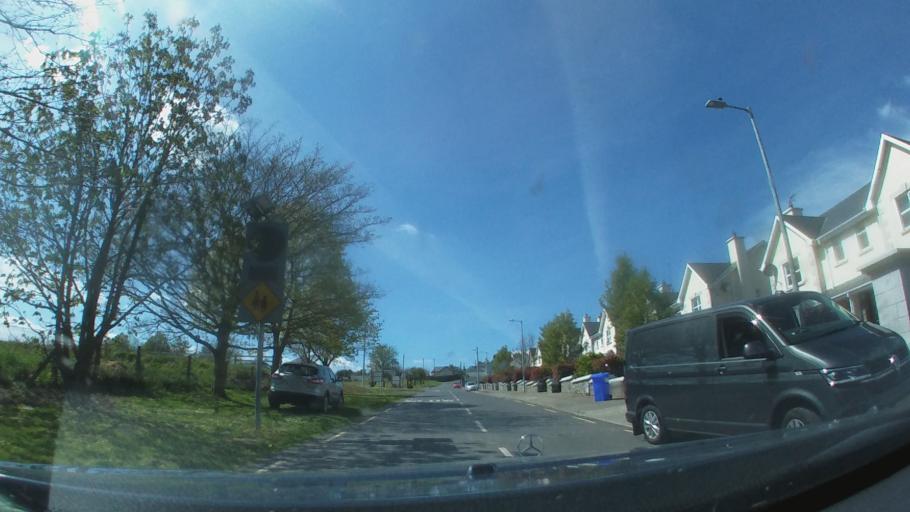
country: IE
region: Leinster
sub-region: Kilkenny
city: Callan
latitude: 52.6208
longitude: -7.4207
